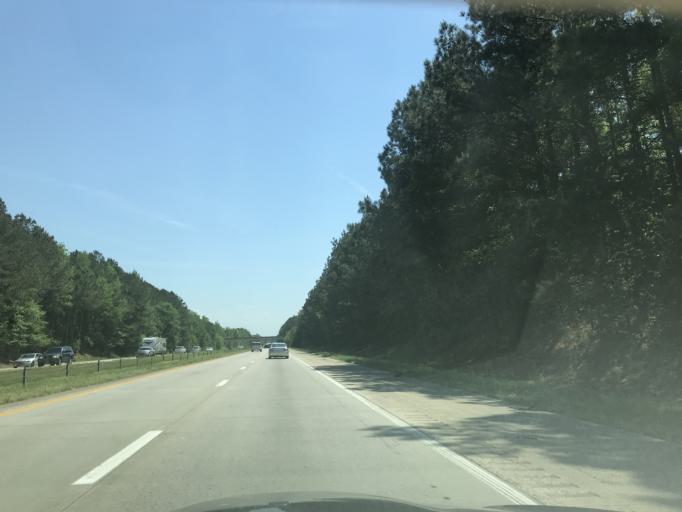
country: US
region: North Carolina
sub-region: Johnston County
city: Benson
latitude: 35.4941
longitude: -78.5532
